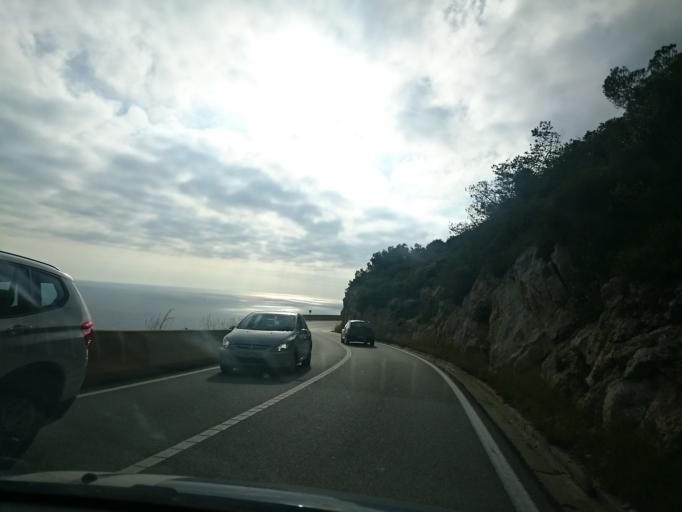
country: ES
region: Catalonia
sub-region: Provincia de Barcelona
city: Sitges
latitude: 41.2484
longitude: 1.8838
